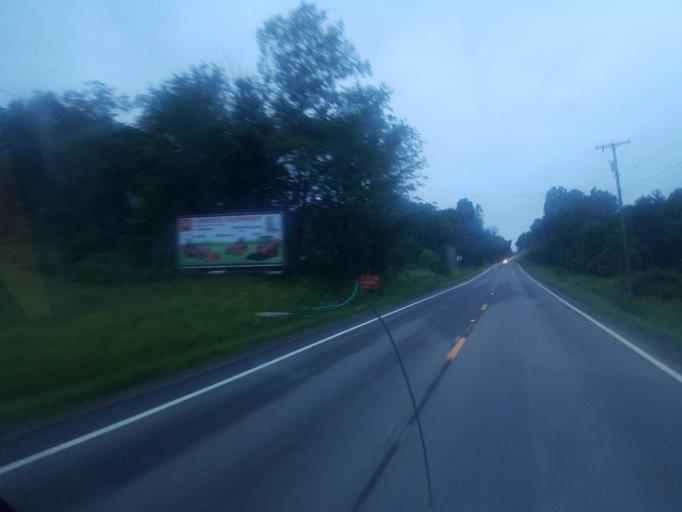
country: US
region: Ohio
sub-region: Carroll County
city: Carrollton
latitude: 40.5414
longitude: -81.0319
